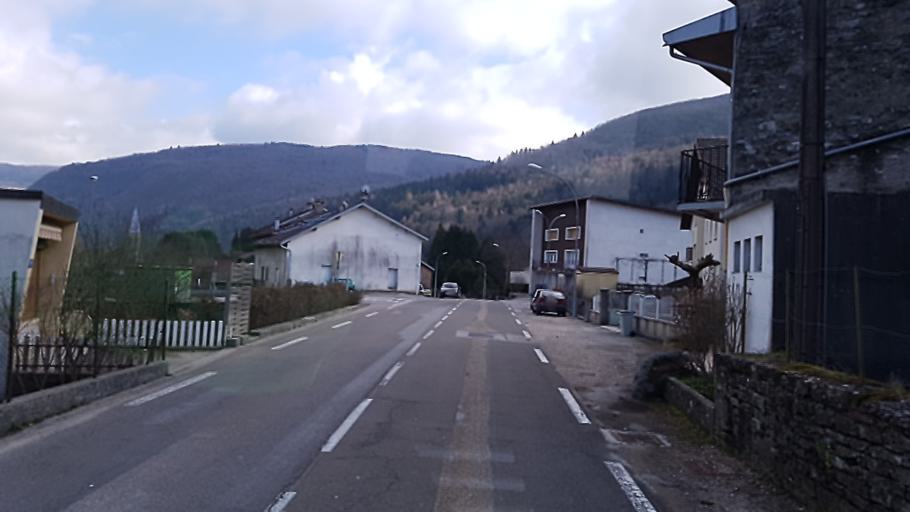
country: FR
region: Franche-Comte
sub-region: Departement du Jura
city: Lavans-les-Saint-Claude
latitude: 46.3596
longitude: 5.7337
